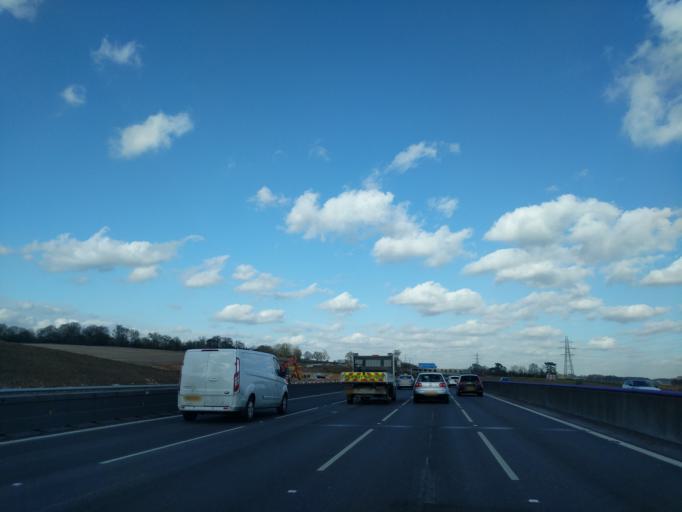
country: GB
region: England
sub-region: Buckinghamshire
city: Chalfont Saint Peter
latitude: 51.6150
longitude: -0.5264
